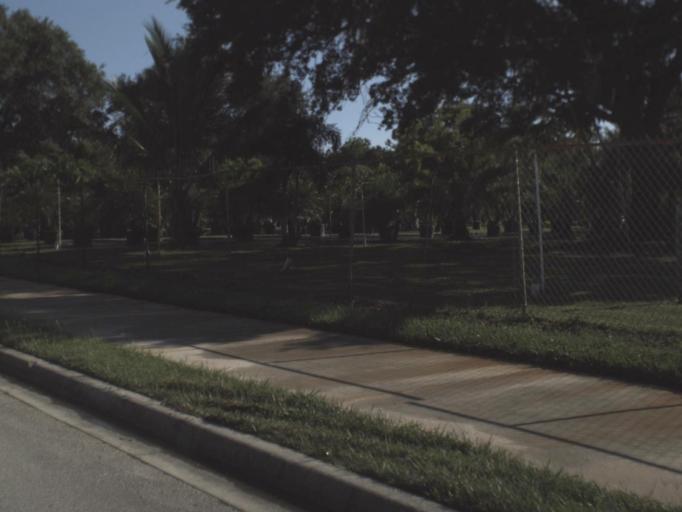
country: US
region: Florida
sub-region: Sarasota County
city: Englewood
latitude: 26.9857
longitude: -82.3640
